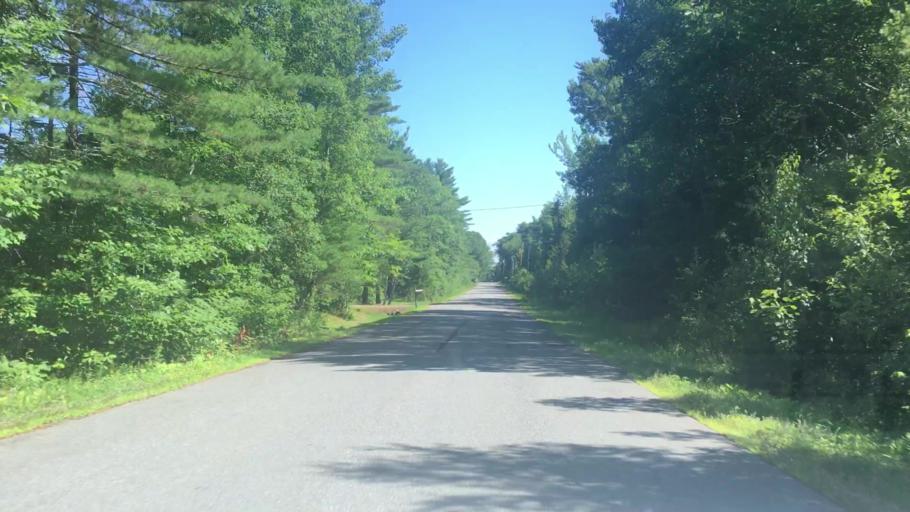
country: US
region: Maine
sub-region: Waldo County
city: Northport
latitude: 44.3757
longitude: -68.9829
